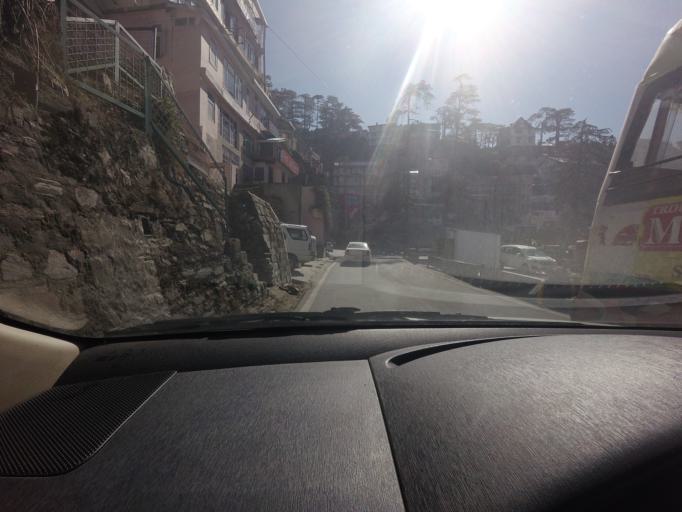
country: IN
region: Himachal Pradesh
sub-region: Shimla
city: Shimla
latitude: 31.1069
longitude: 77.1655
